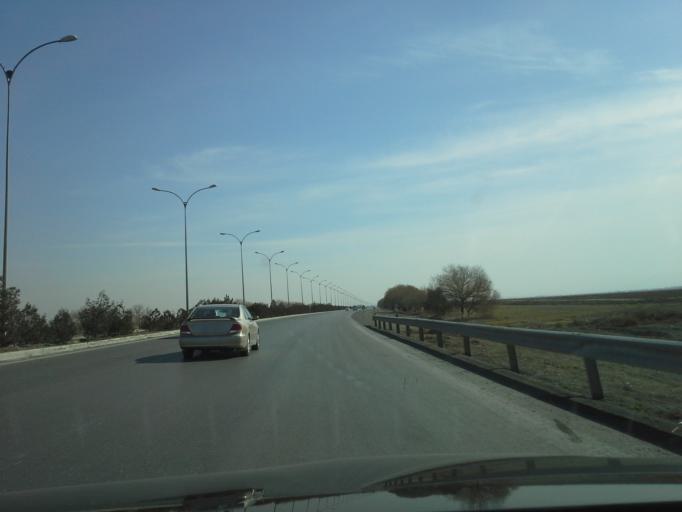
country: TM
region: Ahal
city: Abadan
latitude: 38.1336
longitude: 58.0167
